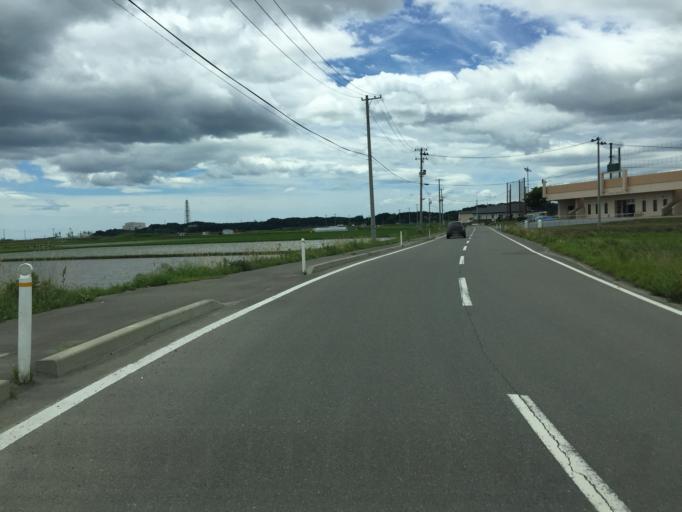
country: JP
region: Fukushima
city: Namie
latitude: 37.6958
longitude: 140.9919
